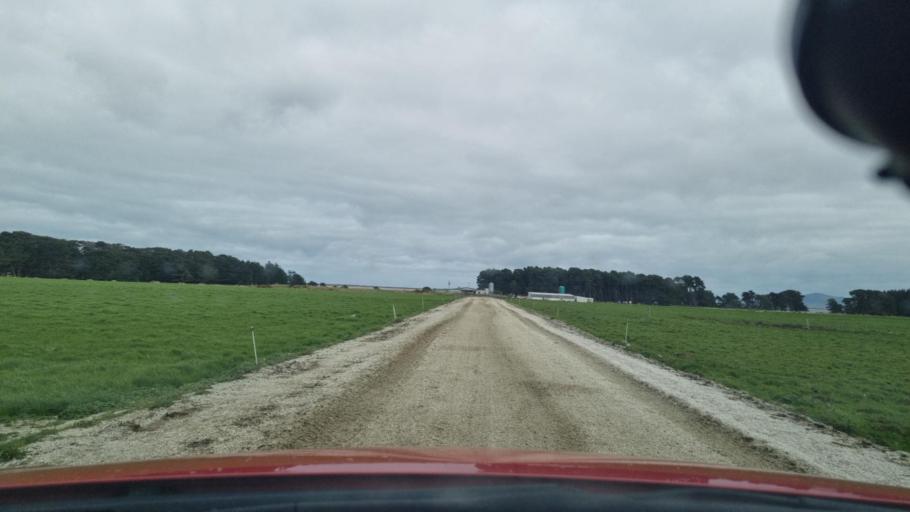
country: NZ
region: Southland
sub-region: Invercargill City
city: Bluff
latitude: -46.5619
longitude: 168.4910
